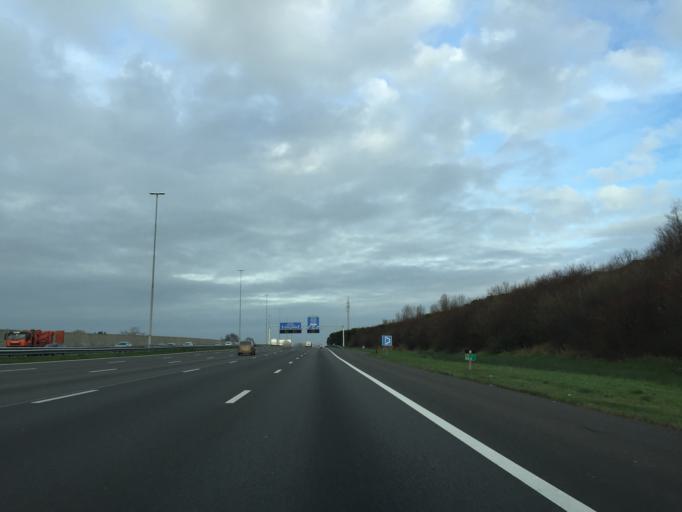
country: NL
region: Utrecht
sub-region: Gemeente Nieuwegein
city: Nieuwegein
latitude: 52.0376
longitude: 5.0644
